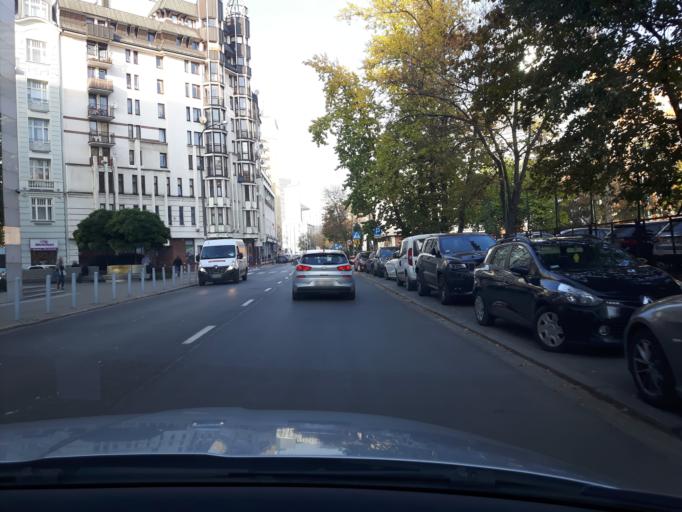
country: PL
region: Masovian Voivodeship
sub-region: Warszawa
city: Wola
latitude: 52.2301
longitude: 20.9951
